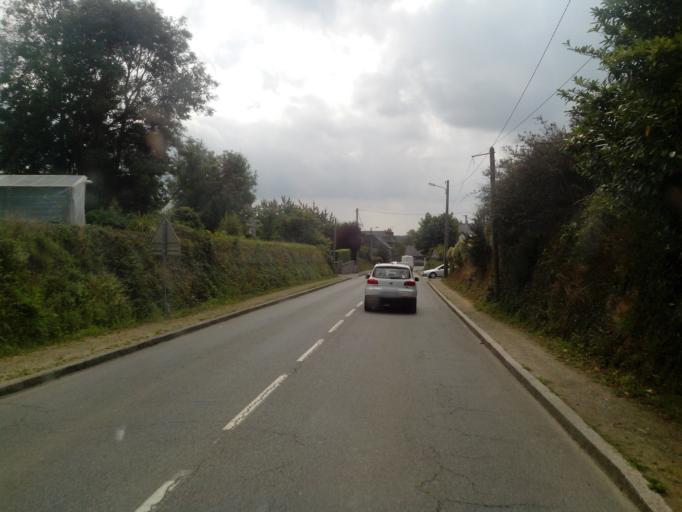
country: FR
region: Brittany
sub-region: Departement des Cotes-d'Armor
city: Plouha
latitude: 48.6774
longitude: -2.9311
